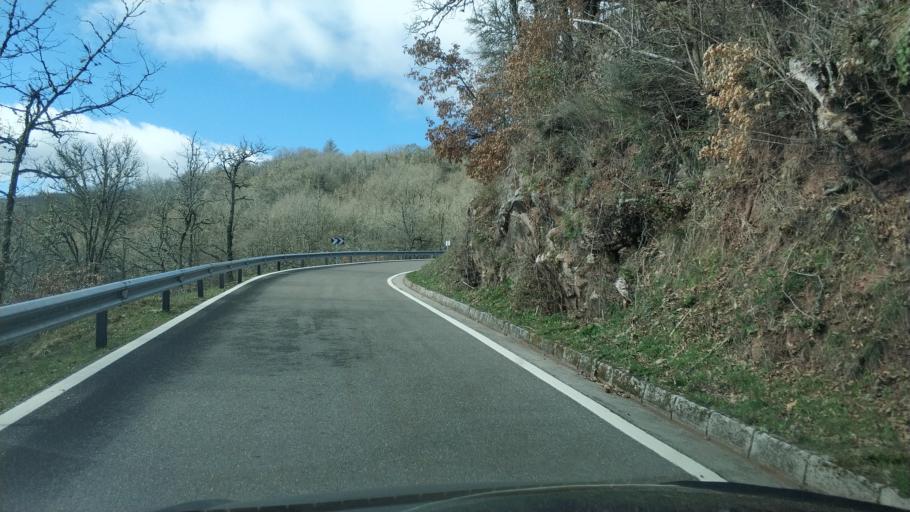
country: ES
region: Castille and Leon
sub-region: Provincia de Palencia
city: Berzosilla
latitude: 42.8991
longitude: -4.0387
